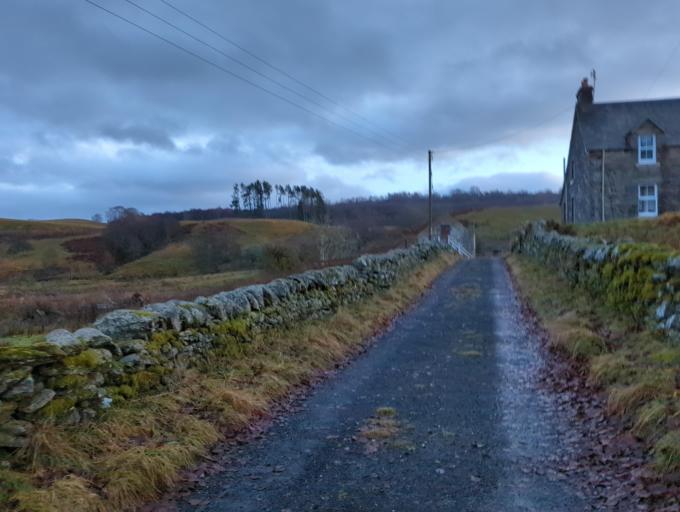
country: GB
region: Scotland
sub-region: Perth and Kinross
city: Bankfoot
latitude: 56.5484
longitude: -3.6325
